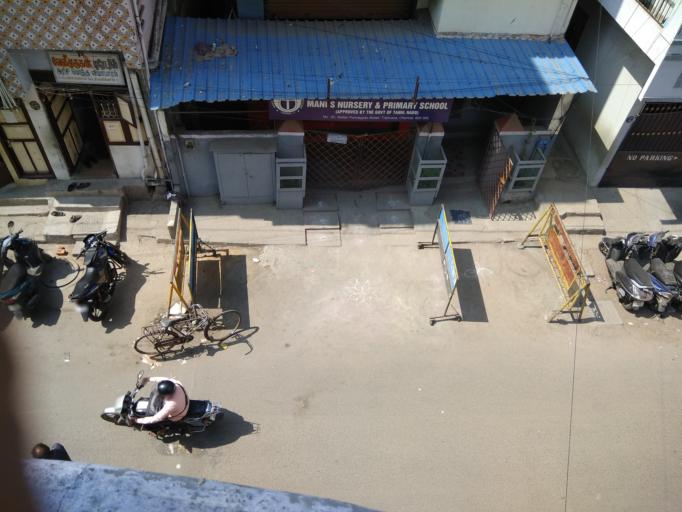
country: IN
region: Tamil Nadu
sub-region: Chennai
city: Chennai
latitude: 13.0560
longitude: 80.2721
